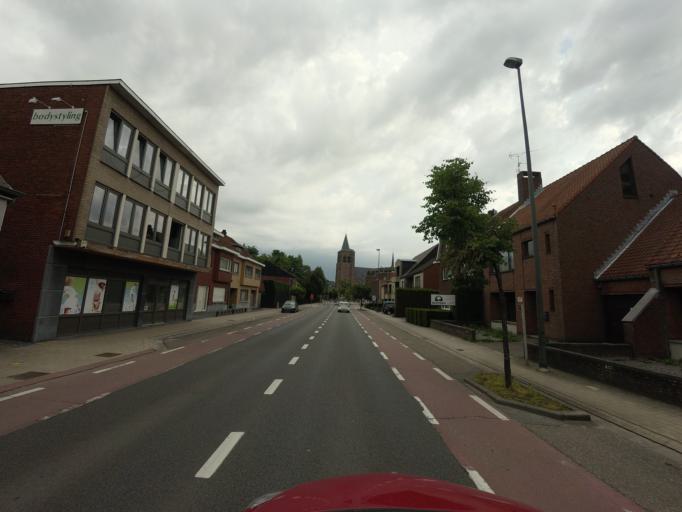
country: BE
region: Flanders
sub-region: Provincie Limburg
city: Lommel
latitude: 51.2266
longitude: 5.3143
